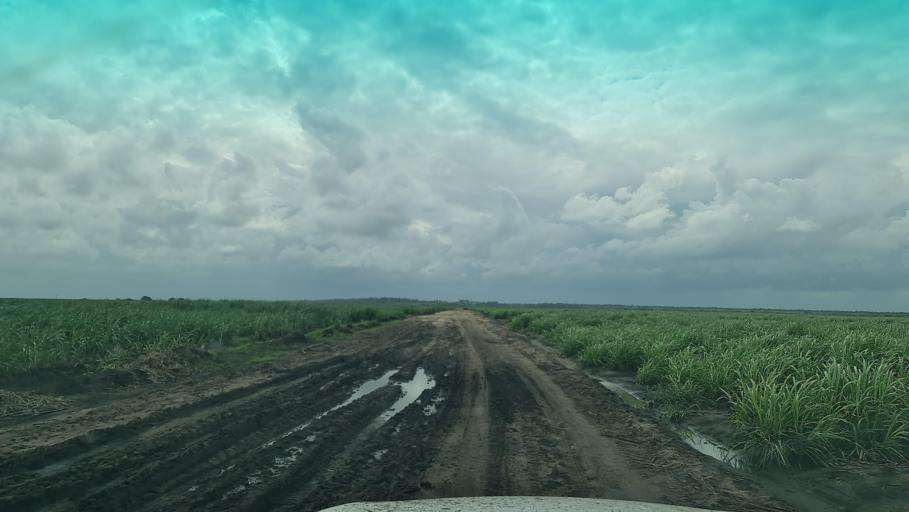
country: MZ
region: Maputo
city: Manhica
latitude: -25.4527
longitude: 32.8245
